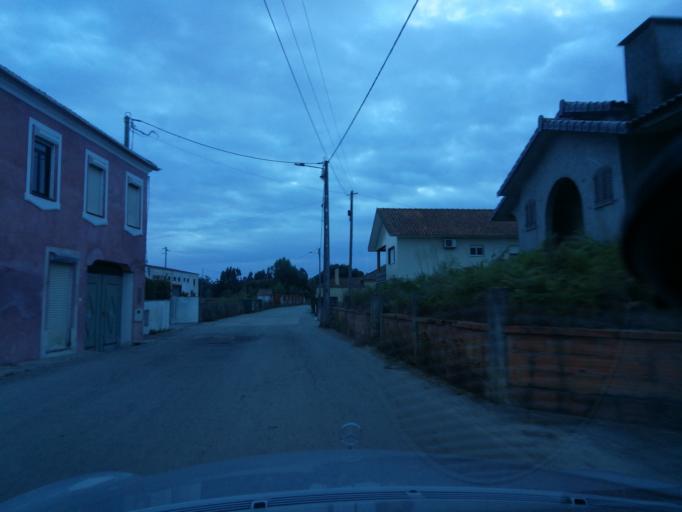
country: PT
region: Aveiro
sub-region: Estarreja
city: Estarreja
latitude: 40.7659
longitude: -8.5971
